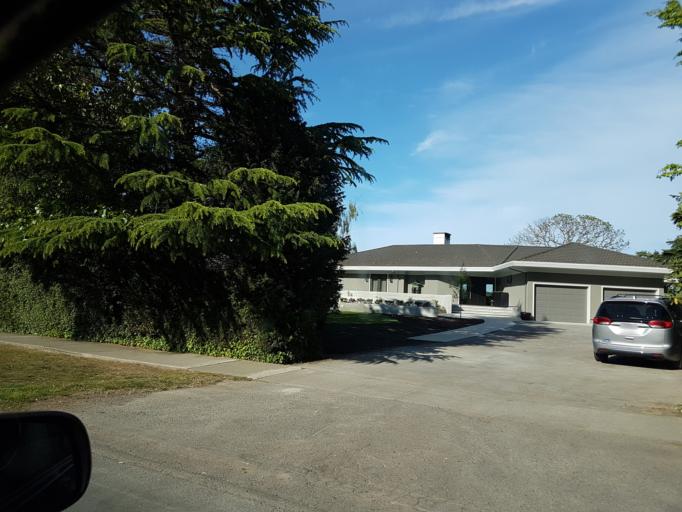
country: CA
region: British Columbia
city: Oak Bay
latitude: 48.4467
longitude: -123.2942
